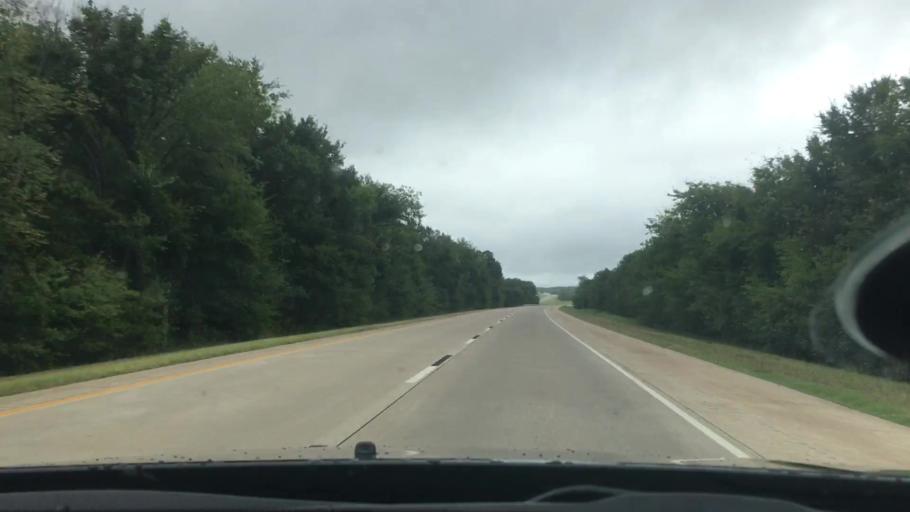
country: US
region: Oklahoma
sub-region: Okmulgee County
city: Henryetta
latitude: 35.4317
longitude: -95.8859
